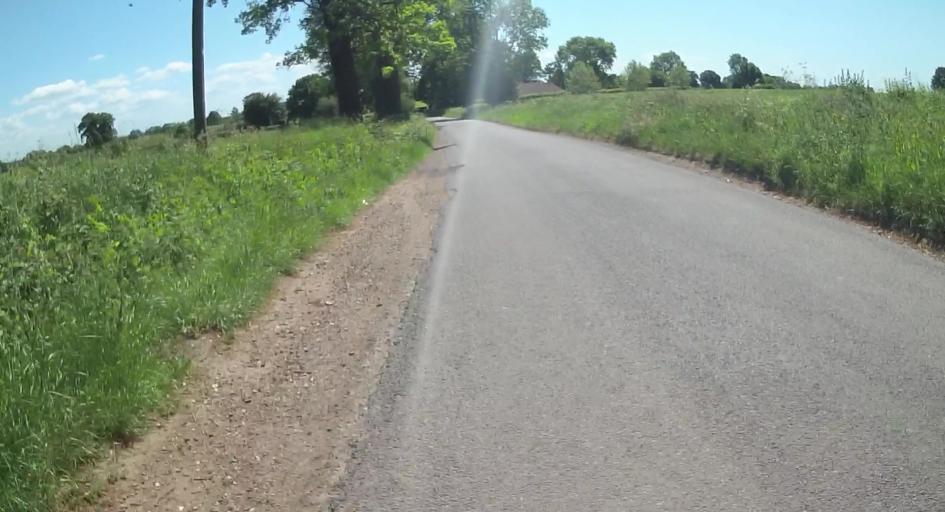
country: GB
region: England
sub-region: West Berkshire
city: Stratfield Mortimer
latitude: 51.3524
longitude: -1.0444
